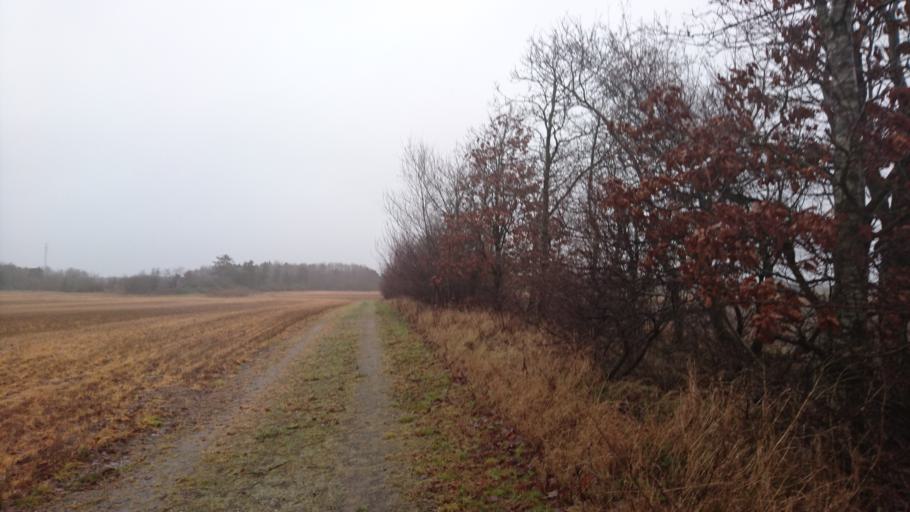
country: DK
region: Central Jutland
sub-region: Herning Kommune
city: Sunds
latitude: 56.1934
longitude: 9.0281
